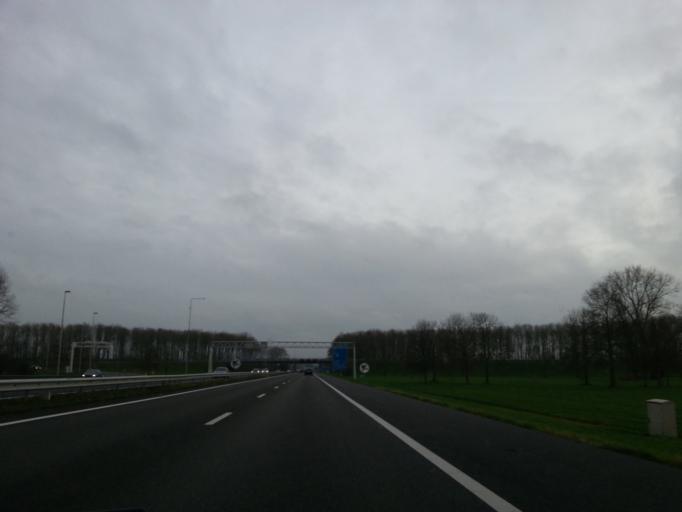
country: NL
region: Gelderland
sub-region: Gemeente Zevenaar
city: Zevenaar
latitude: 51.9158
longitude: 6.1370
